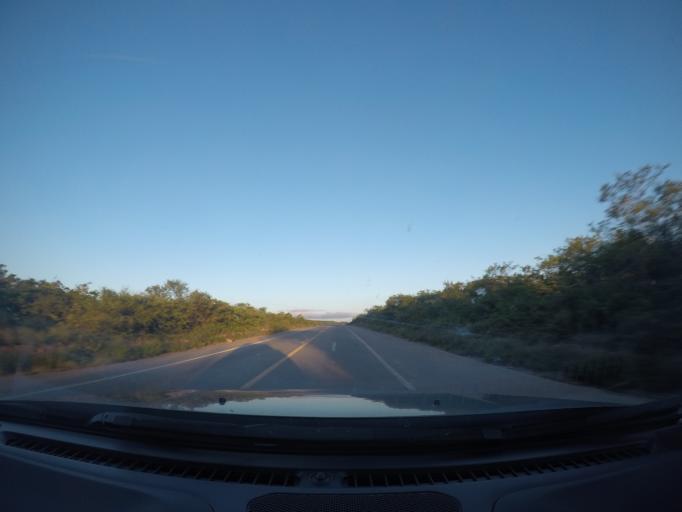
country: BR
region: Bahia
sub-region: Seabra
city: Seabra
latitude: -12.3908
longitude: -41.9050
